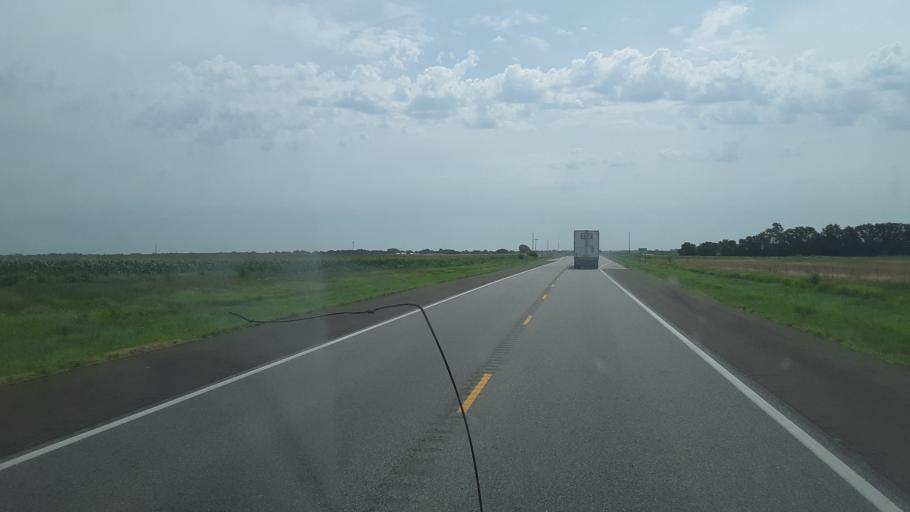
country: US
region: Kansas
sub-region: Reno County
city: South Hutchinson
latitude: 37.9850
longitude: -98.0909
